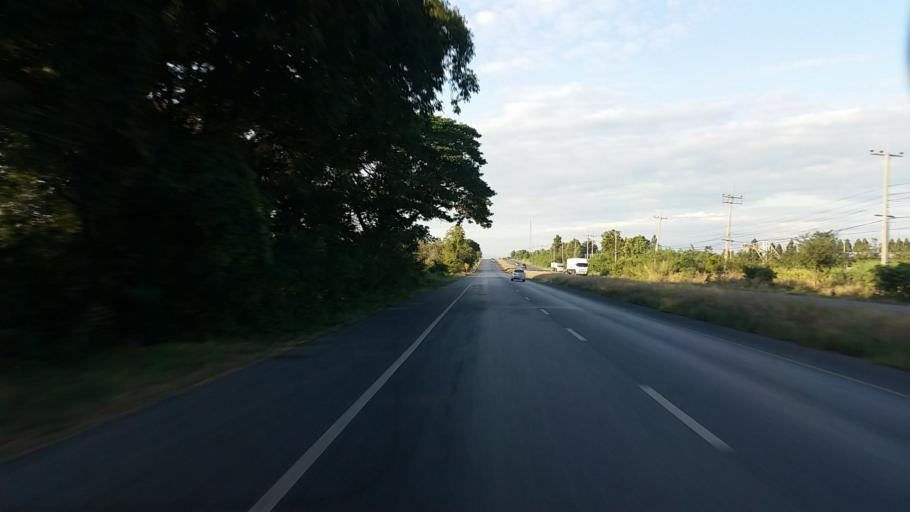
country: TH
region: Lop Buri
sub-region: Amphoe Tha Luang
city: Tha Luang
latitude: 15.0550
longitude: 100.9678
